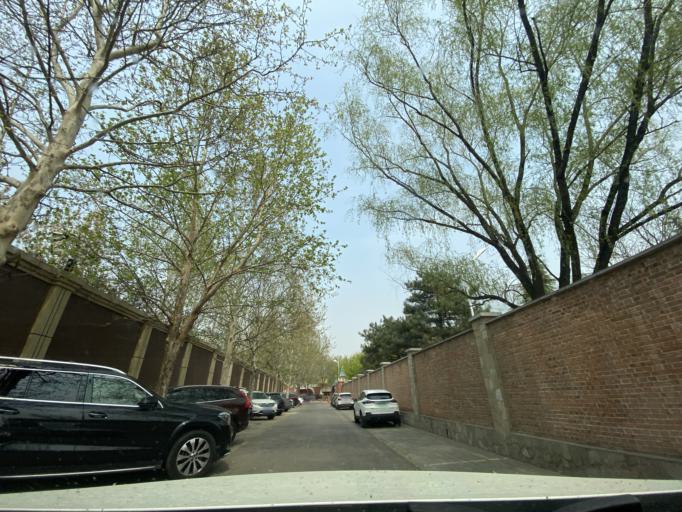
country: CN
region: Beijing
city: Sijiqing
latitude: 39.9421
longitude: 116.2458
